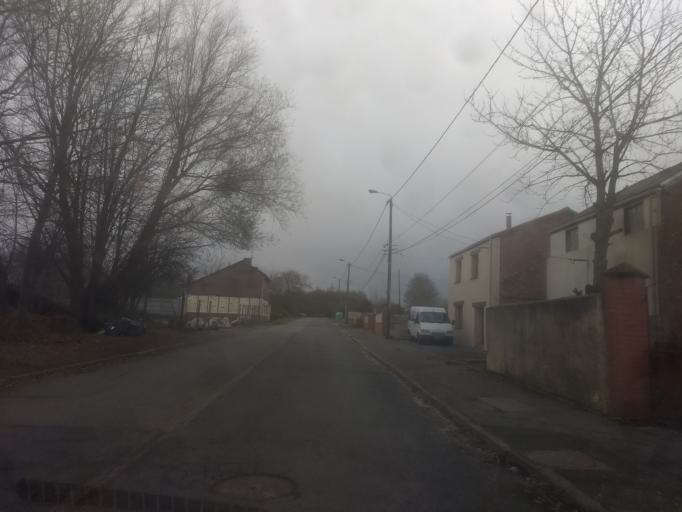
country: FR
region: Nord-Pas-de-Calais
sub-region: Departement du Pas-de-Calais
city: Lievin
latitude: 50.4089
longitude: 2.7780
